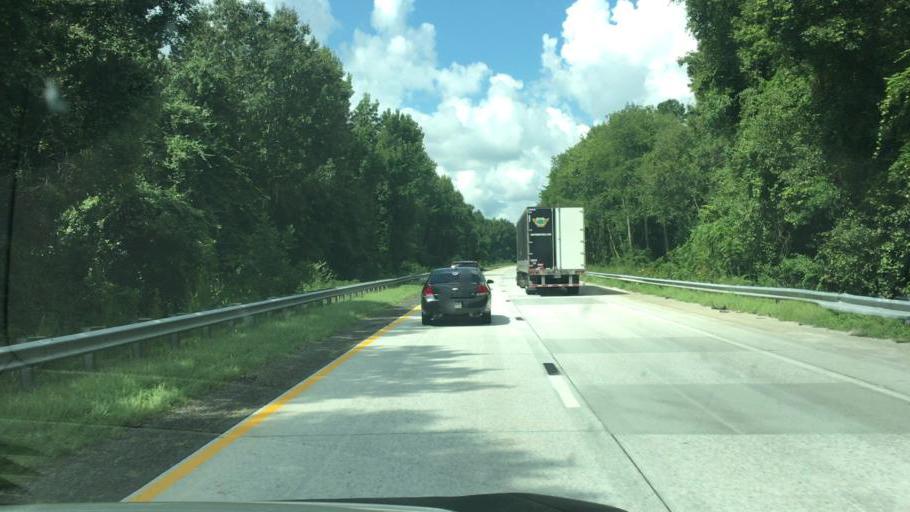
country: US
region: South Carolina
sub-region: Florence County
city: Florence
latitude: 34.2927
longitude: -79.6475
